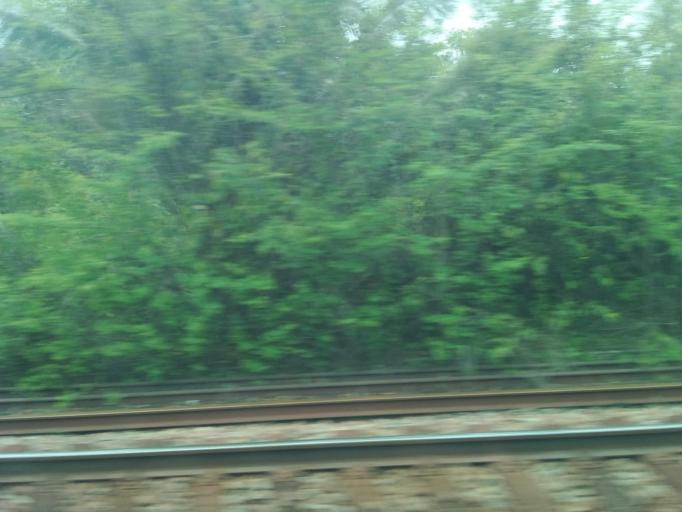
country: BR
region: Maranhao
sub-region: Santa Ines
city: Santa Ines
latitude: -3.6525
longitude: -45.7967
